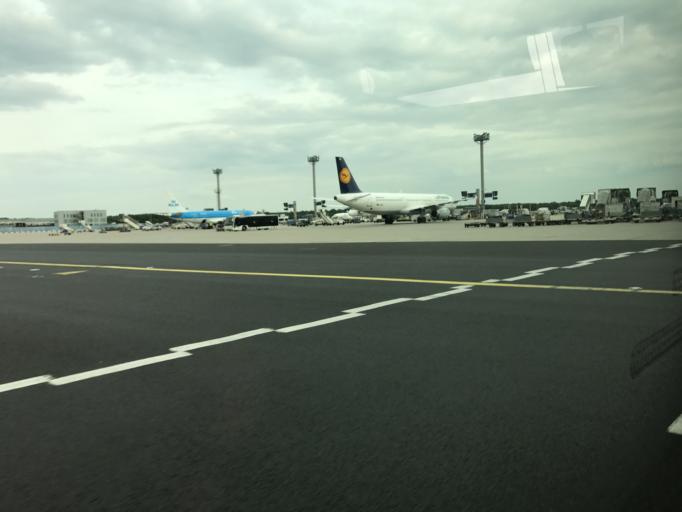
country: DE
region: Hesse
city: Niederrad
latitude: 50.0504
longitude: 8.5895
